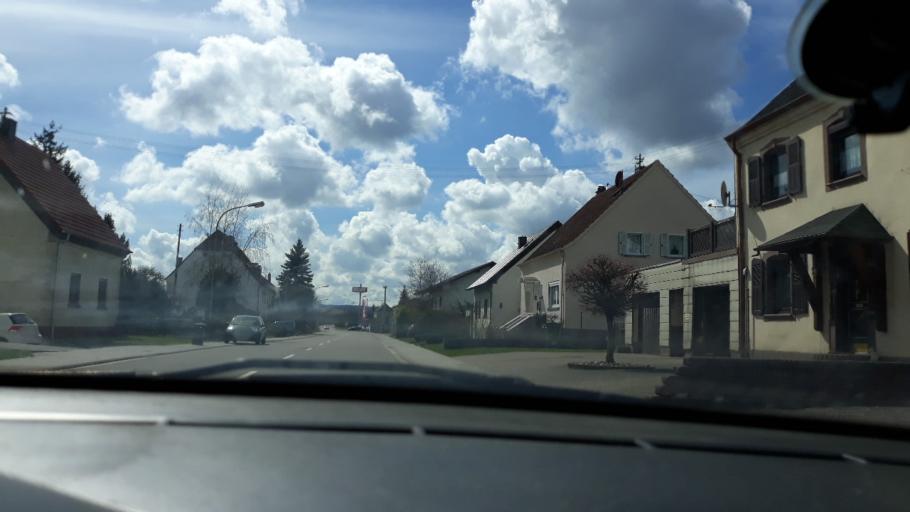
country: DE
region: Saarland
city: Gersheim
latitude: 49.1456
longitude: 7.2038
